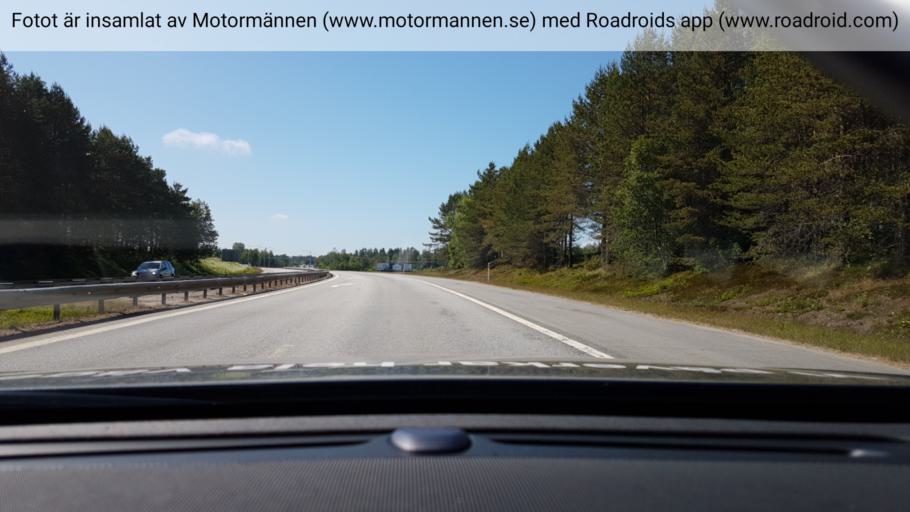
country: SE
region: Vaesterbotten
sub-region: Umea Kommun
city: Roback
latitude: 63.7815
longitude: 20.1939
